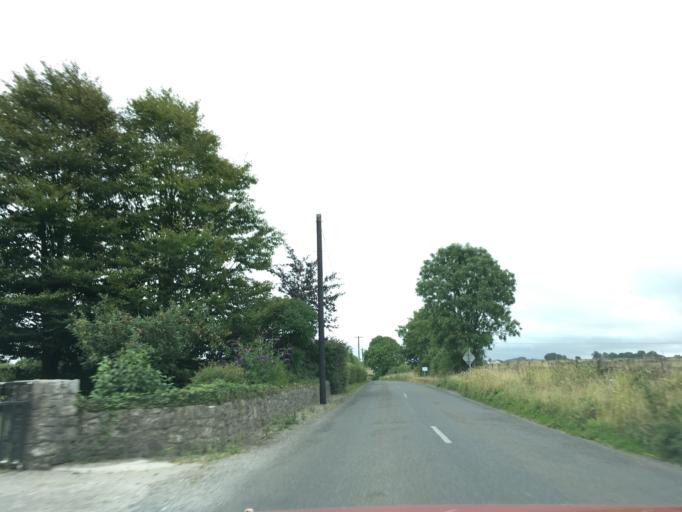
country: IE
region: Munster
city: Cashel
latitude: 52.4752
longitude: -7.8724
